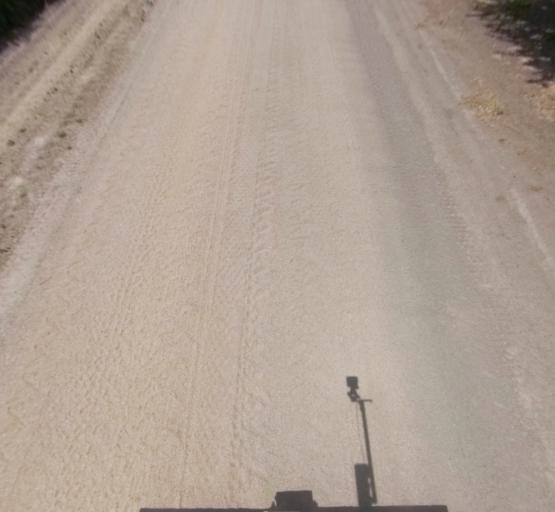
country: US
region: California
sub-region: Fresno County
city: Kerman
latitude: 36.8221
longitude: -120.1768
